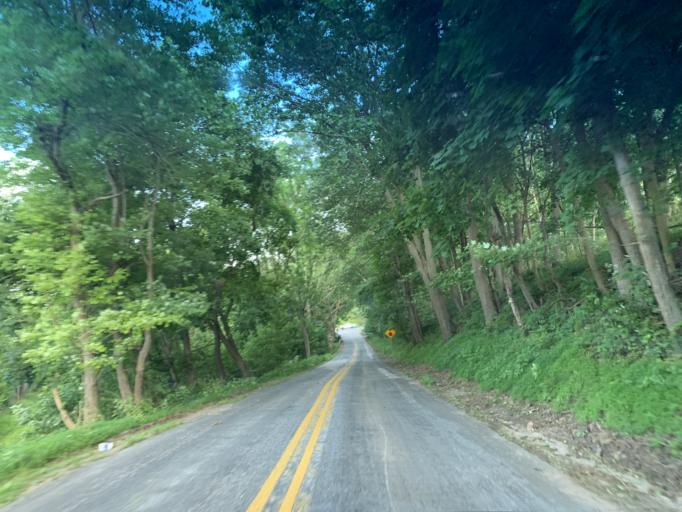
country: US
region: Pennsylvania
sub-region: York County
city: Stewartstown
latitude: 39.7518
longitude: -76.5376
